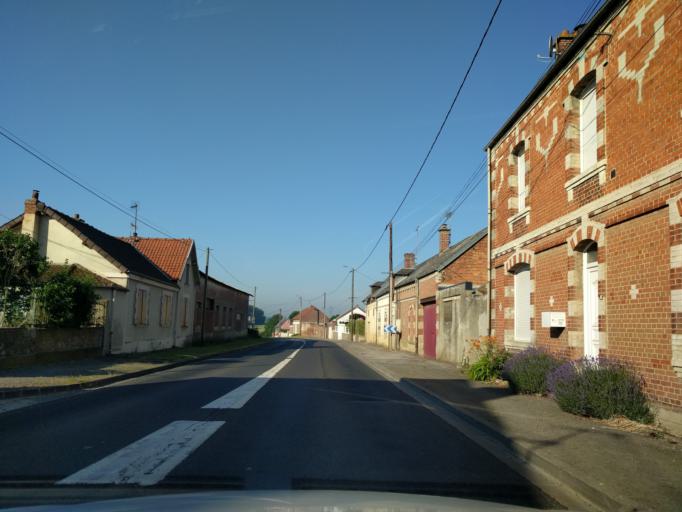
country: FR
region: Picardie
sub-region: Departement de la Somme
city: Chaulnes
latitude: 49.8335
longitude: 2.8639
